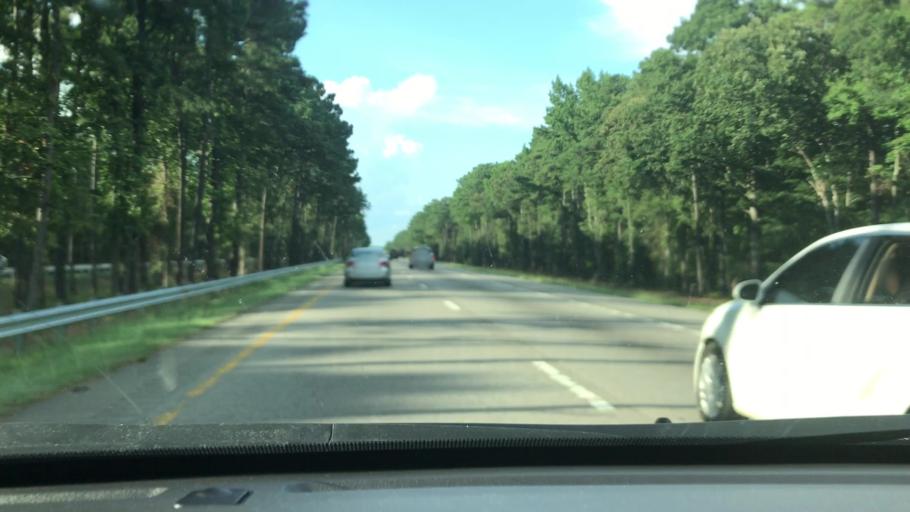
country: US
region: North Carolina
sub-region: Robeson County
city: Lumberton
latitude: 34.6816
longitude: -79.0021
